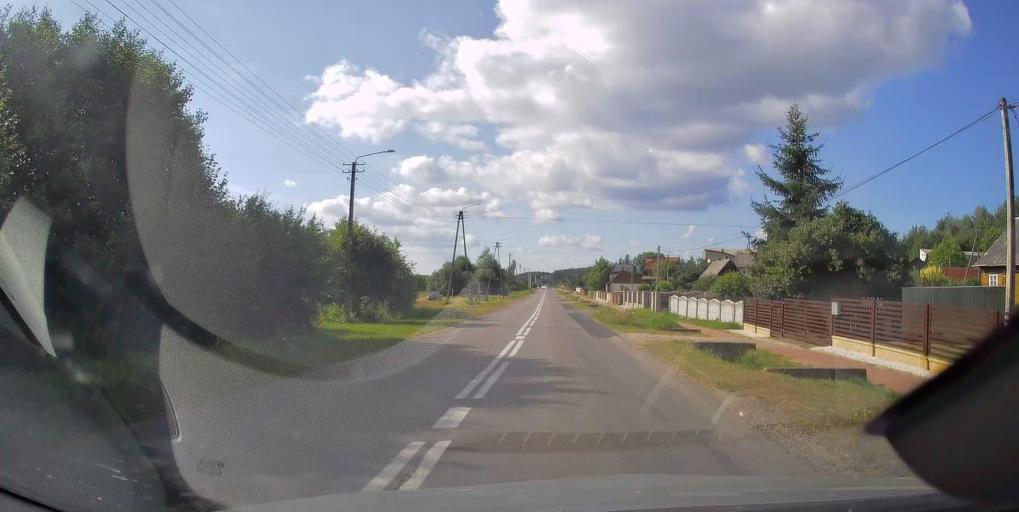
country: PL
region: Swietokrzyskie
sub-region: Powiat skarzyski
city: Suchedniow
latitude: 51.0025
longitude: 20.8496
